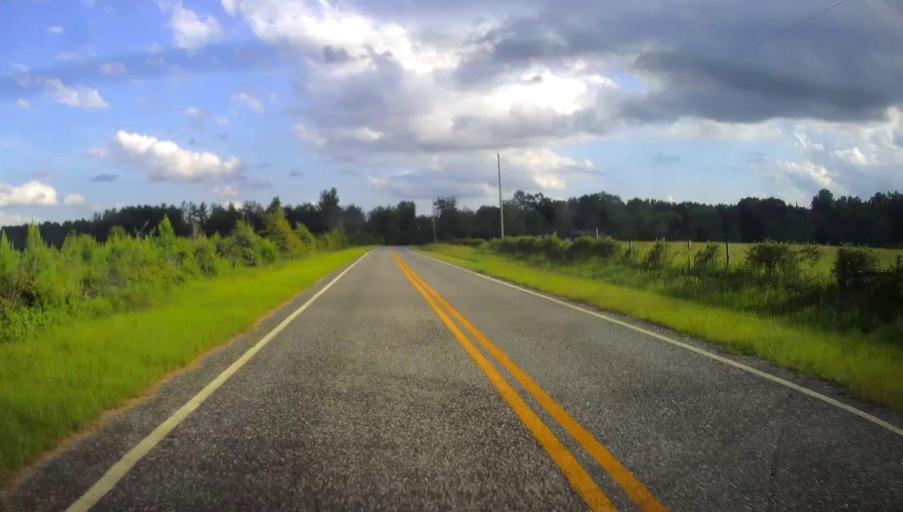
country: US
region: Georgia
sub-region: Crawford County
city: Roberta
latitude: 32.7072
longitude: -84.0167
